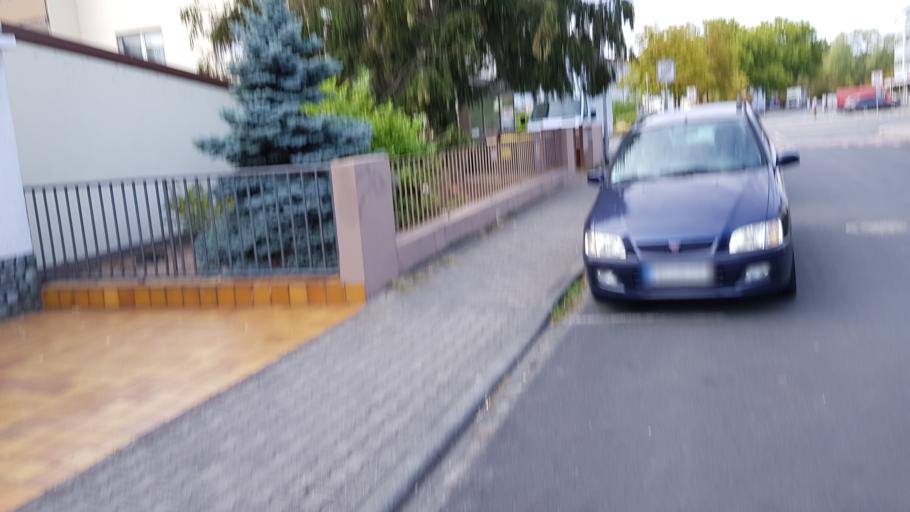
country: DE
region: Hesse
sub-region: Regierungsbezirk Darmstadt
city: Russelsheim
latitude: 49.9976
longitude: 8.4297
